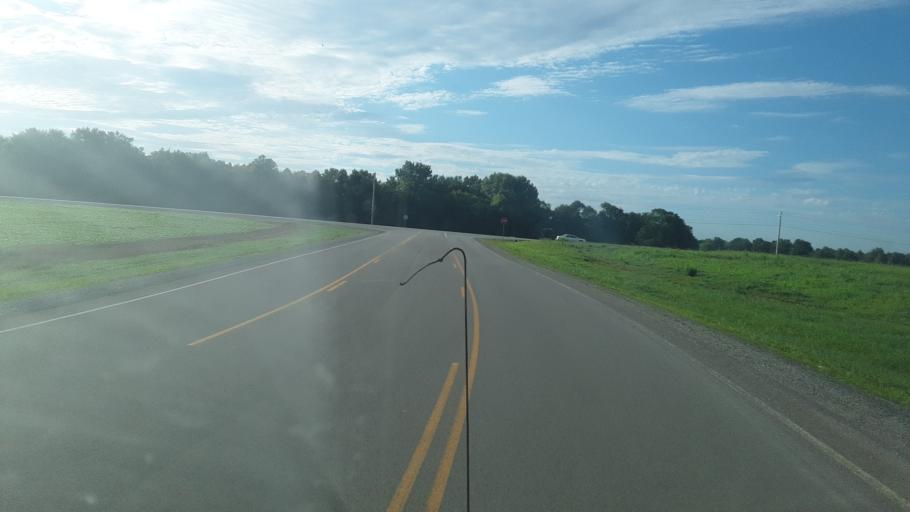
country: US
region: Kentucky
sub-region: Todd County
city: Guthrie
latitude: 36.6642
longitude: -87.1695
